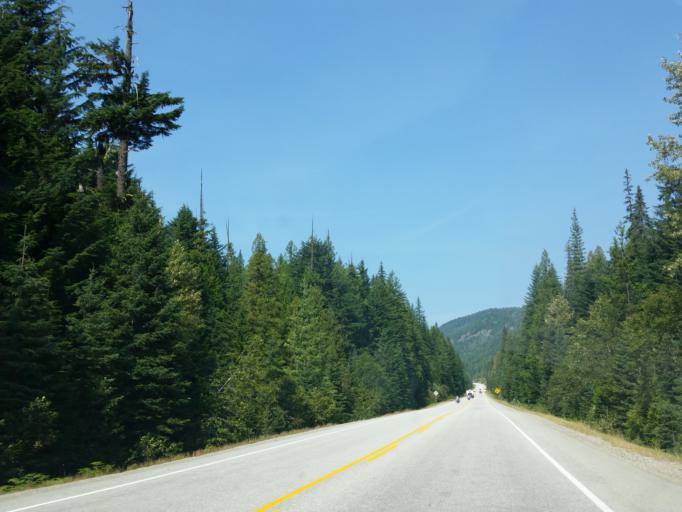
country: CA
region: British Columbia
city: Castlegar
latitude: 49.2867
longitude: -117.7442
